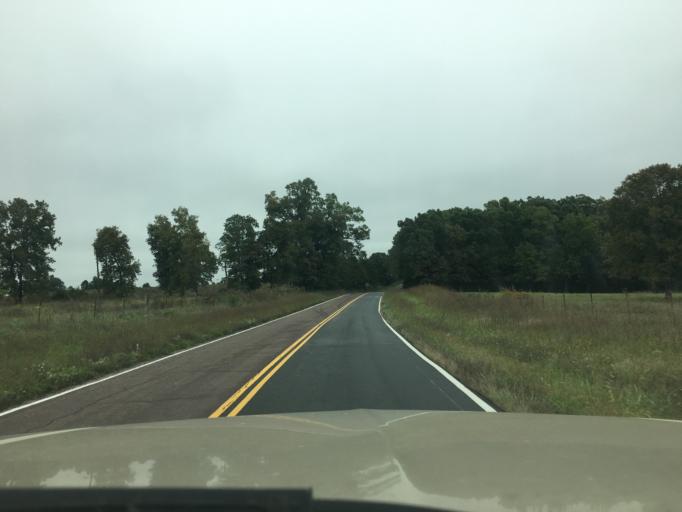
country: US
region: Missouri
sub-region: Crawford County
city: Cuba
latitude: 38.1804
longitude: -91.4891
